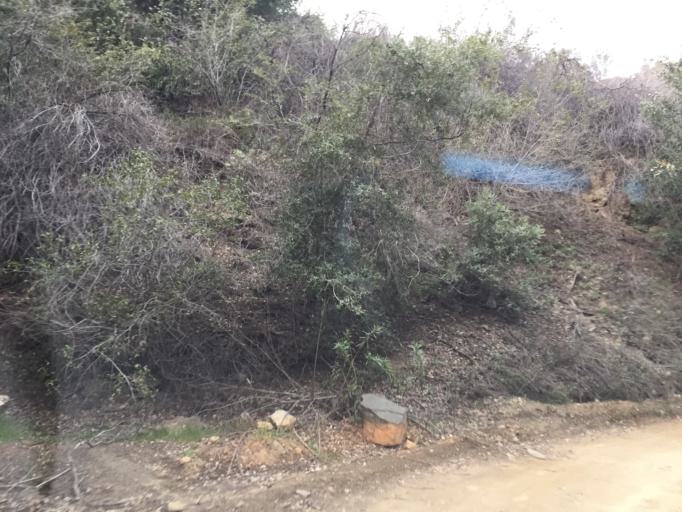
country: US
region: California
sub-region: San Bernardino County
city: Yucaipa
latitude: 34.1021
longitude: -117.0264
